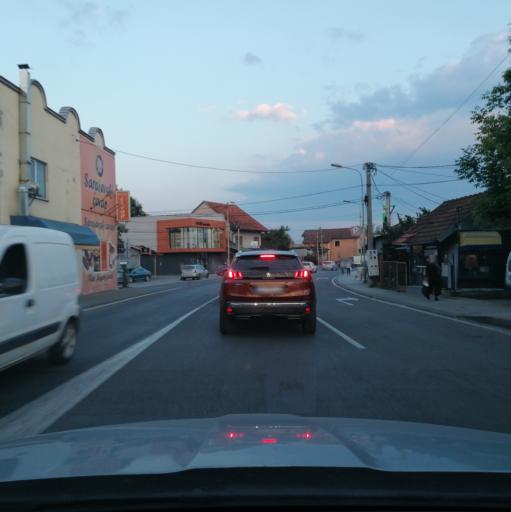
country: RS
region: Central Serbia
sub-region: Raski Okrug
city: Kraljevo
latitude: 43.7173
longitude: 20.6907
